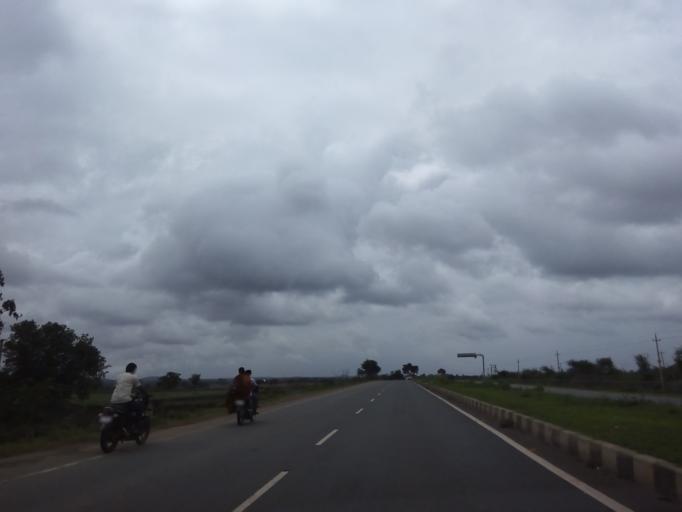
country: IN
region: Karnataka
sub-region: Haveri
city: Haveri
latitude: 14.7721
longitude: 75.4226
